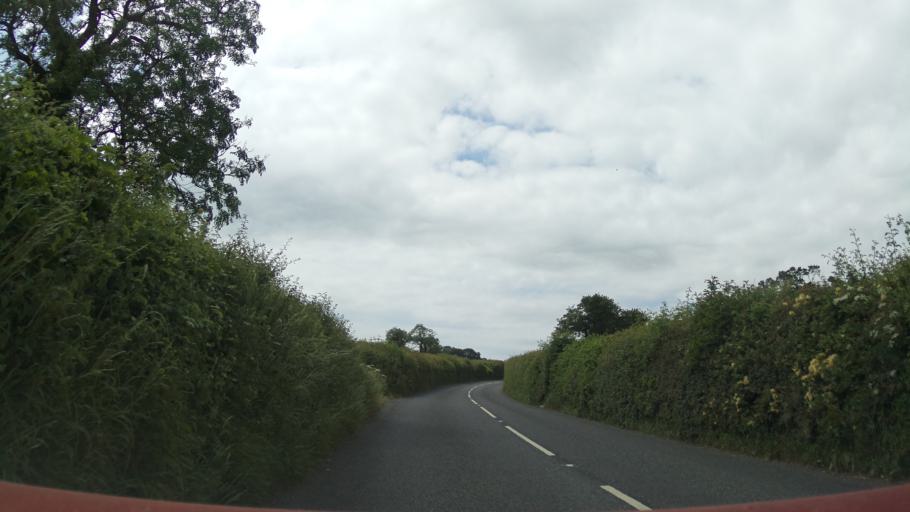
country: GB
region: England
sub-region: Somerset
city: Milborne Port
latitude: 51.0261
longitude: -2.4621
